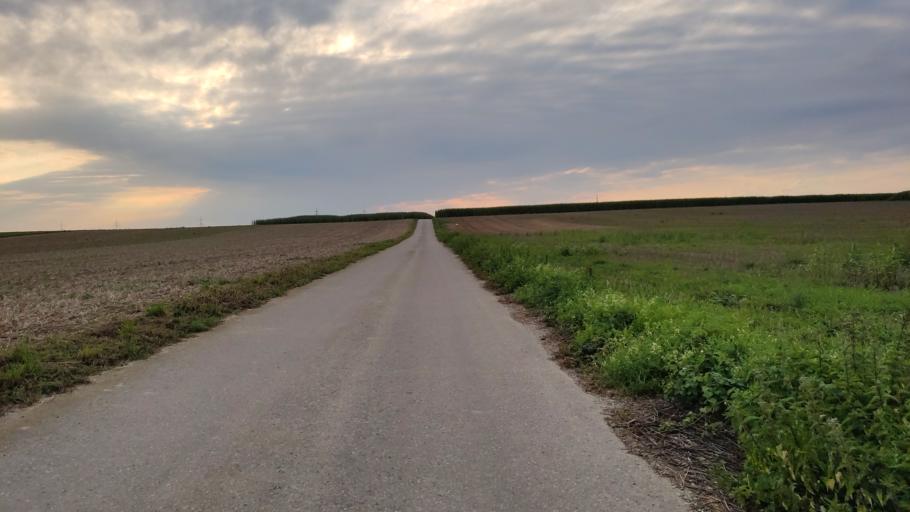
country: DE
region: Bavaria
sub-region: Swabia
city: Oberottmarshausen
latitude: 48.2485
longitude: 10.8649
